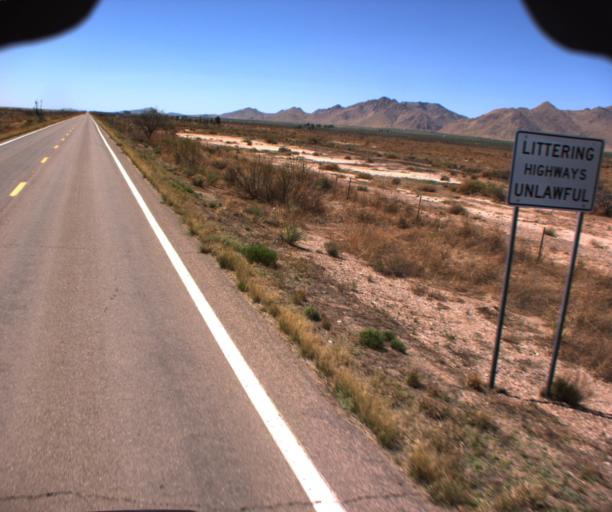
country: US
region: New Mexico
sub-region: Hidalgo County
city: Lordsburg
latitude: 31.8072
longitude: -109.0517
